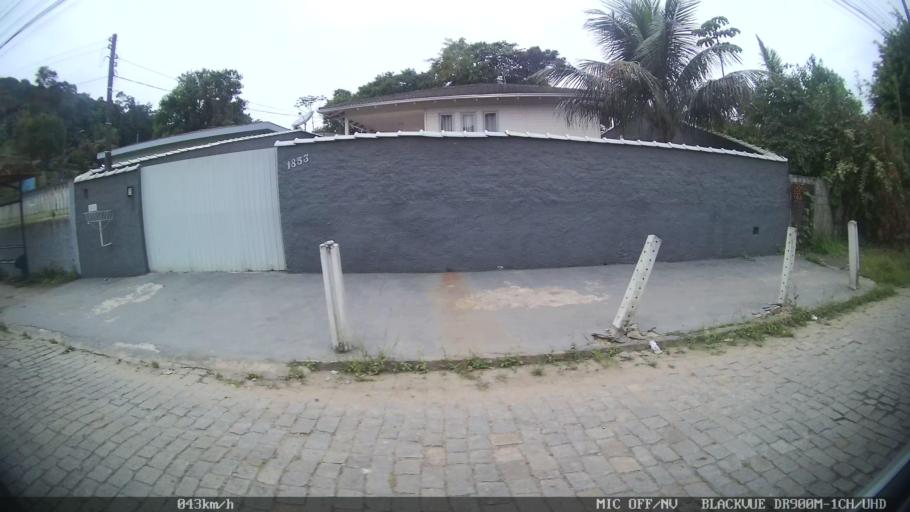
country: BR
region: Santa Catarina
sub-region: Joinville
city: Joinville
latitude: -26.3395
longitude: -48.8573
